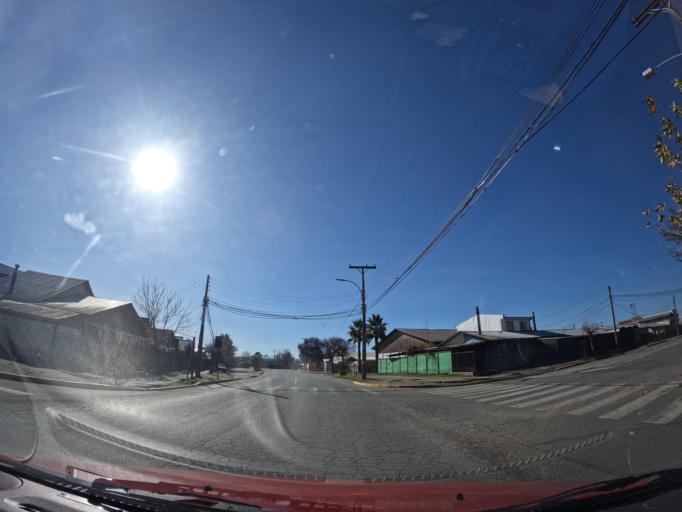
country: CL
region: Maule
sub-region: Provincia de Cauquenes
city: Cauquenes
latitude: -35.9822
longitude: -72.3163
